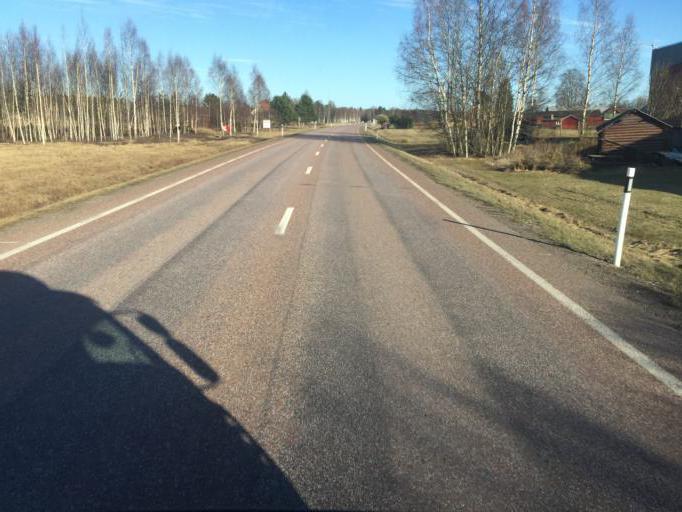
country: SE
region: Dalarna
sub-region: Vansbro Kommun
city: Jarna
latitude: 60.5485
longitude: 14.3696
